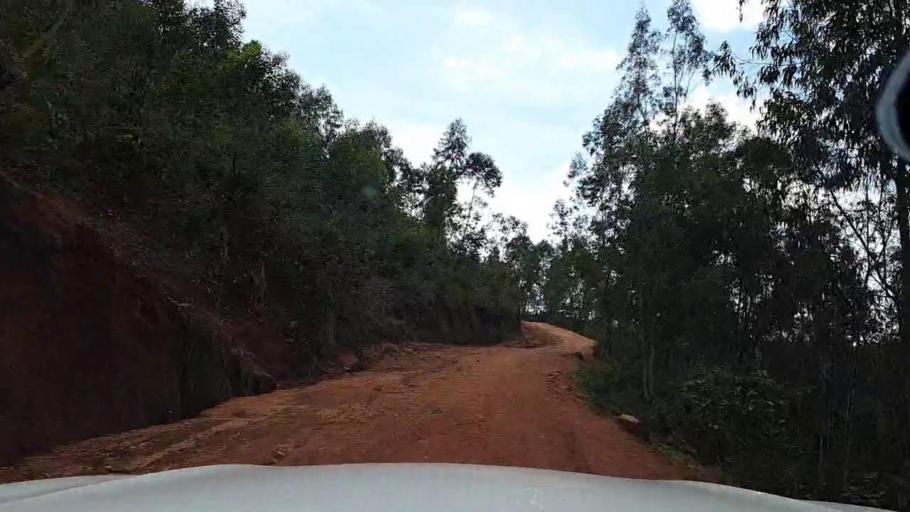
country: RW
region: Southern Province
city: Butare
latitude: -2.7463
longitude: 29.7637
